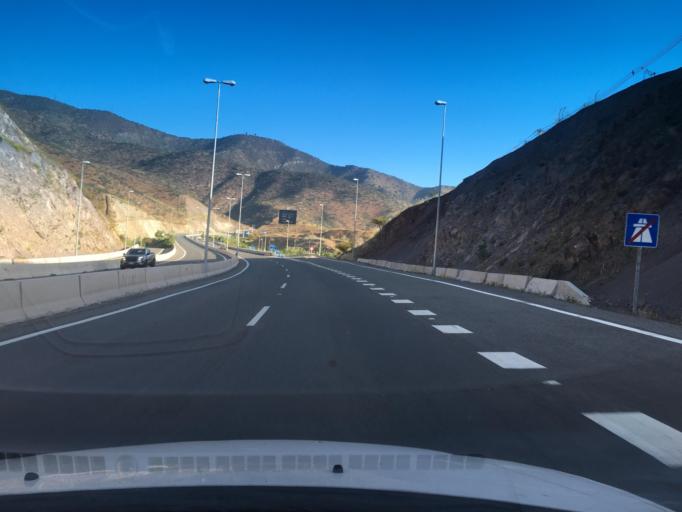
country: CL
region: Santiago Metropolitan
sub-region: Provincia de Chacabuco
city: Chicureo Abajo
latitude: -33.3188
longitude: -70.6270
